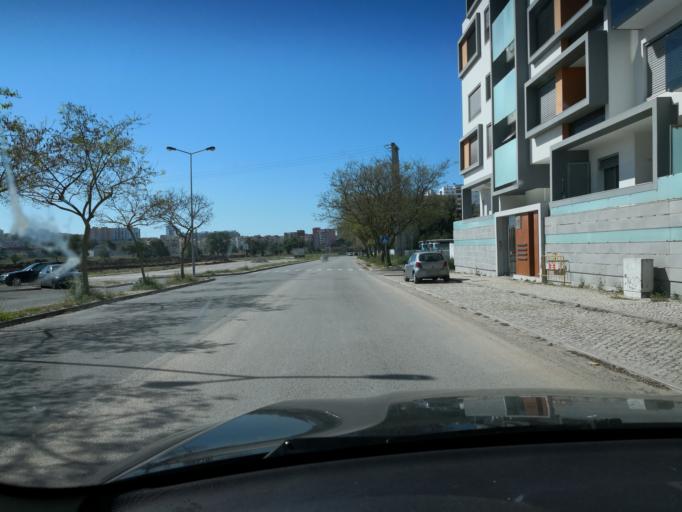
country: PT
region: Setubal
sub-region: Setubal
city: Setubal
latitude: 38.5389
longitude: -8.8897
